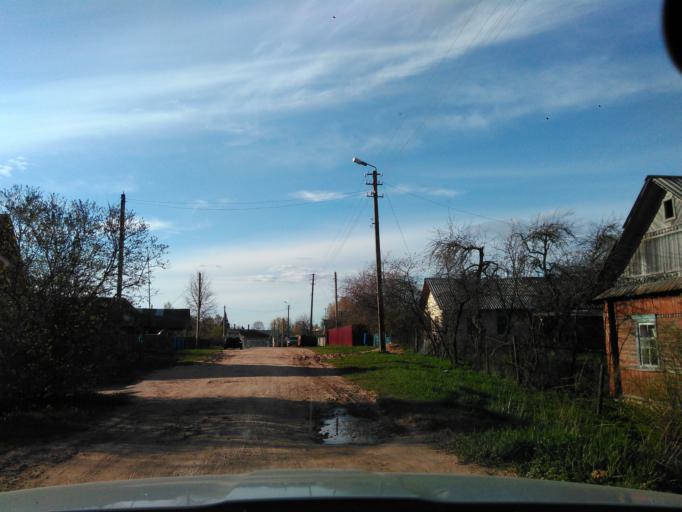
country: BY
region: Vitebsk
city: Chashniki
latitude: 54.8562
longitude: 29.1697
